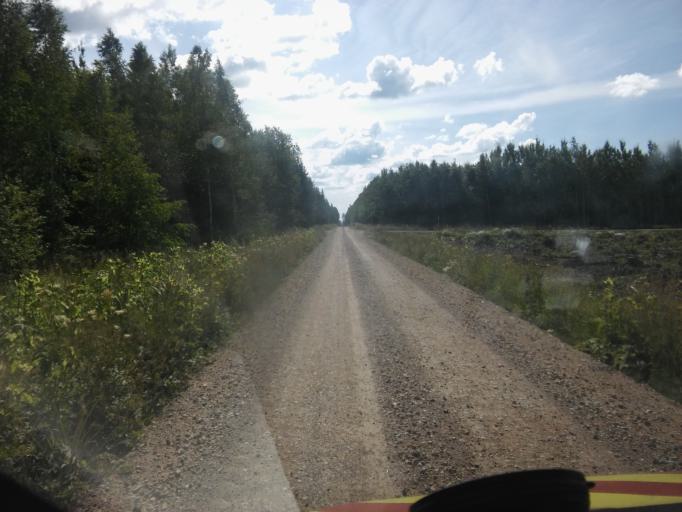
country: EE
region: Paernumaa
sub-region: Sindi linn
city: Sindi
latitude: 58.2671
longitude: 24.7366
